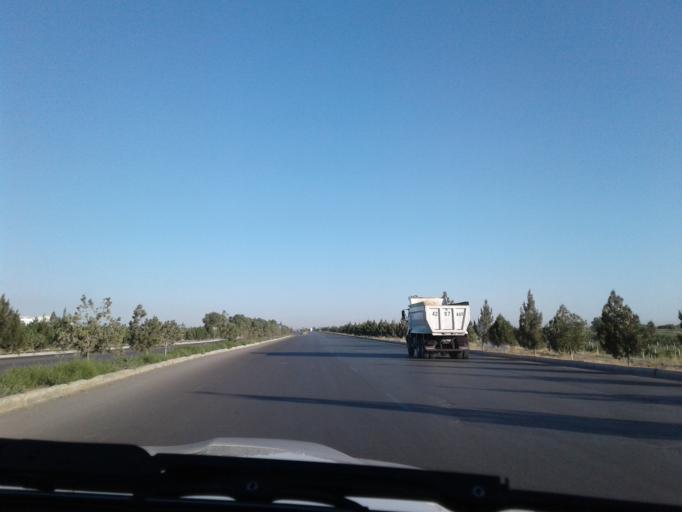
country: TM
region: Ahal
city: Abadan
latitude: 38.0651
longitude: 58.2553
